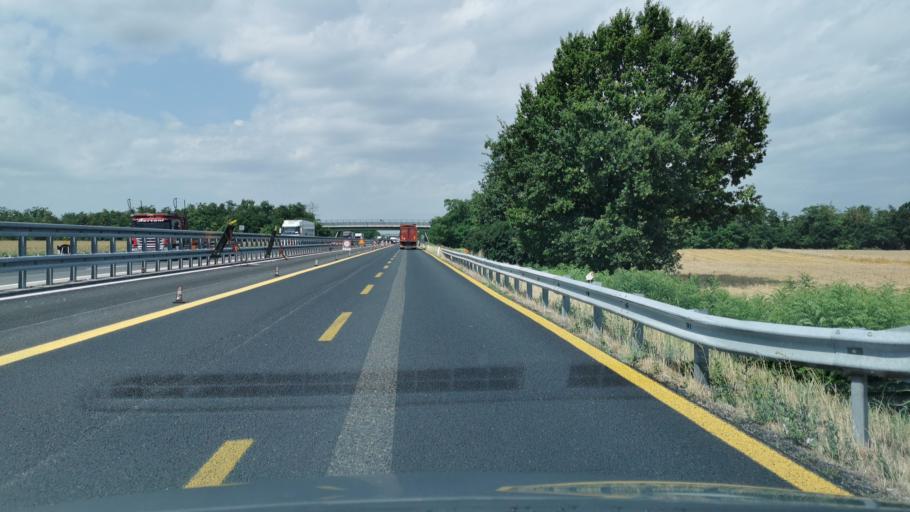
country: IT
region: Lombardy
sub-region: Provincia di Pavia
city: Verretto
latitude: 45.0334
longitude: 9.1159
